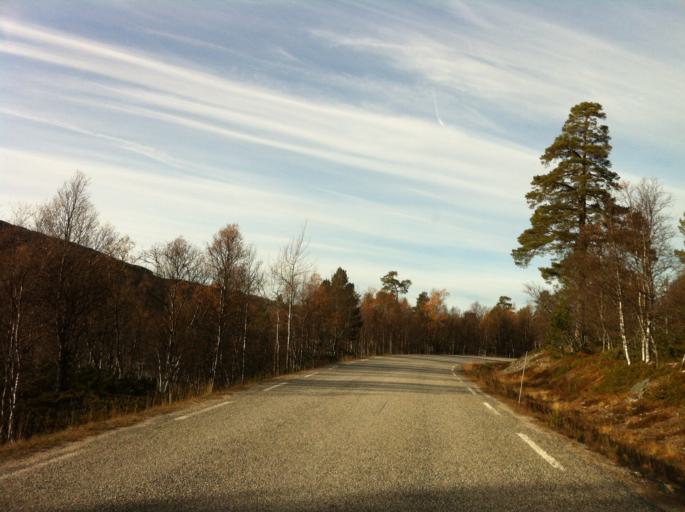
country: NO
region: Hedmark
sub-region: Engerdal
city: Engerdal
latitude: 62.0913
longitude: 12.0445
